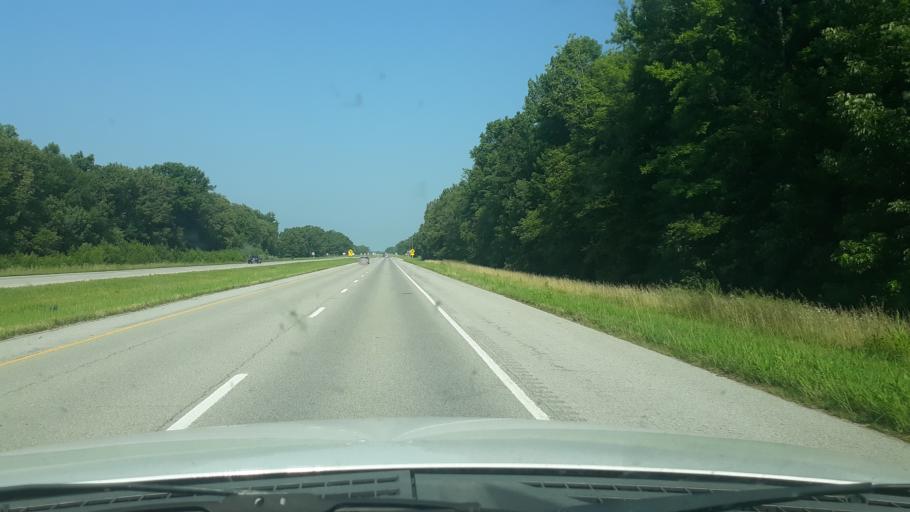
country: US
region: Illinois
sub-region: Saline County
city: Carrier Mills
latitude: 37.7335
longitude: -88.6289
